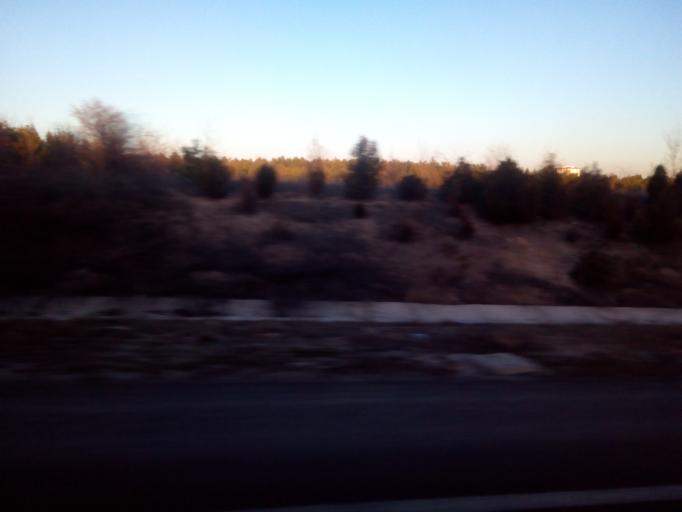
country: TR
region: Ankara
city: Etimesgut
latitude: 40.0180
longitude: 32.6250
